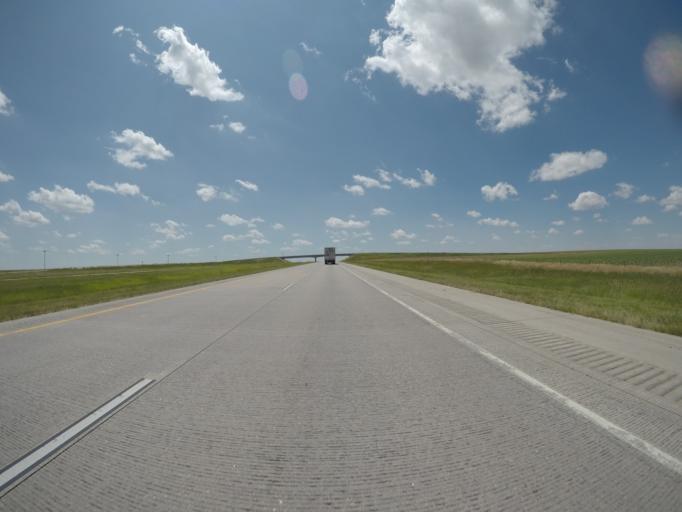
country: US
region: Colorado
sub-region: Lincoln County
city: Hugo
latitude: 39.2778
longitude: -102.9658
